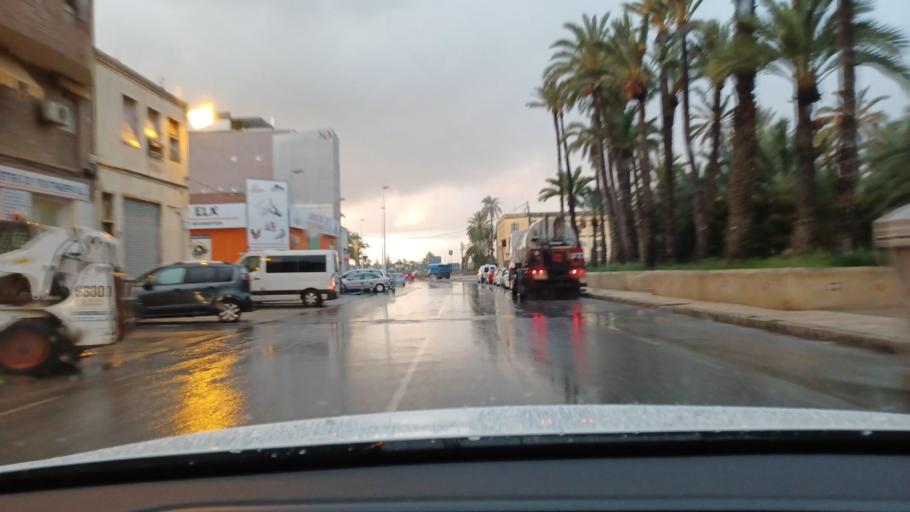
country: ES
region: Valencia
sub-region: Provincia de Alicante
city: Elche
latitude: 38.2550
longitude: -0.6974
